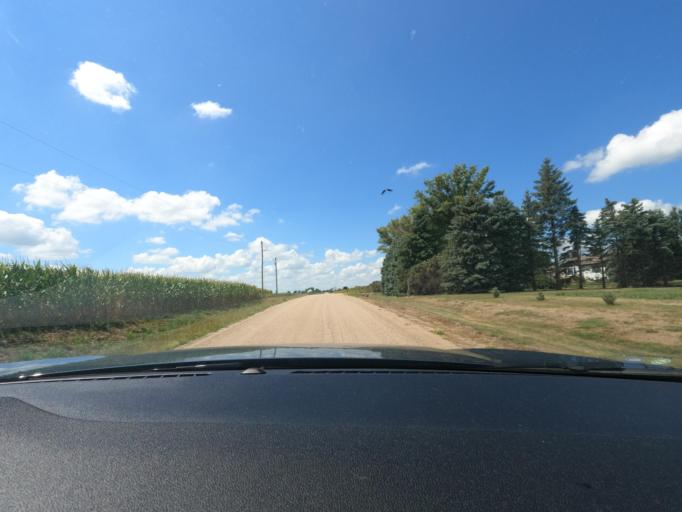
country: US
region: Nebraska
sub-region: Saunders County
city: Wahoo
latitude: 41.2492
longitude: -96.5505
